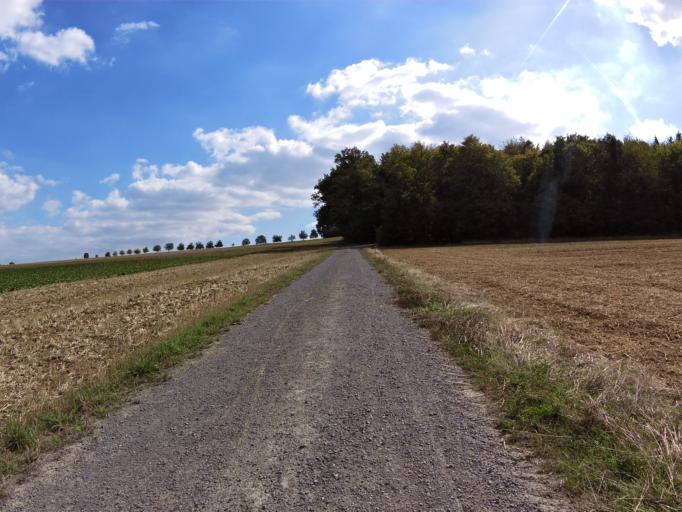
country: DE
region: Bavaria
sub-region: Regierungsbezirk Unterfranken
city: Hettstadt
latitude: 49.7940
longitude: 9.8142
